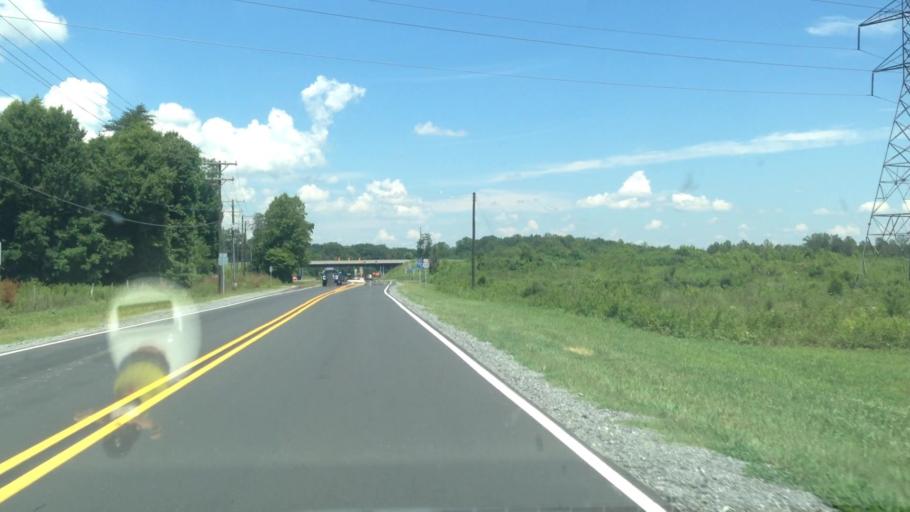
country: US
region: North Carolina
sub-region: Guilford County
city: Summerfield
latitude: 36.2443
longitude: -79.9245
